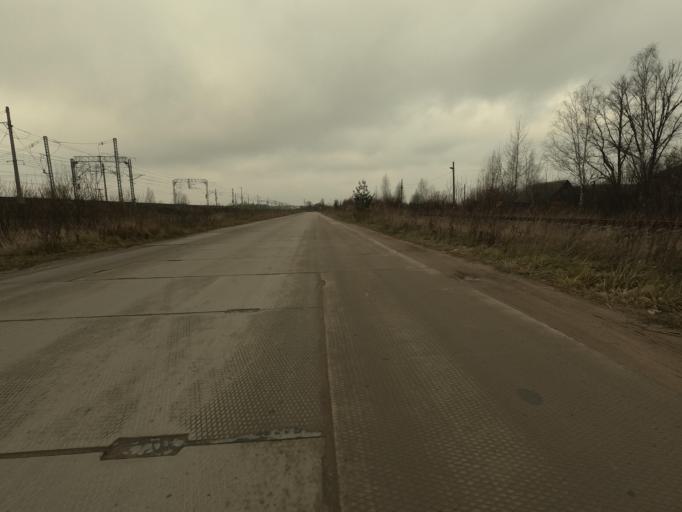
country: RU
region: Leningrad
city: Lyuban'
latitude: 59.4765
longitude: 31.2569
